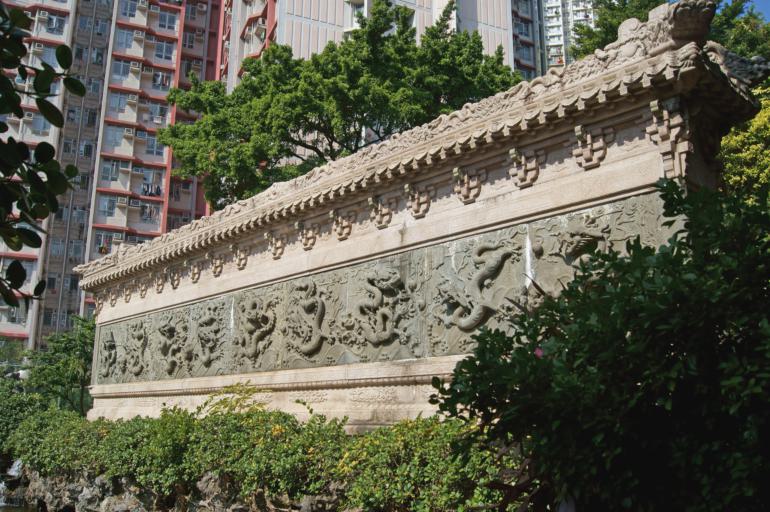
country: HK
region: Wong Tai Sin
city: Wong Tai Sin
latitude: 22.3429
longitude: 114.1932
